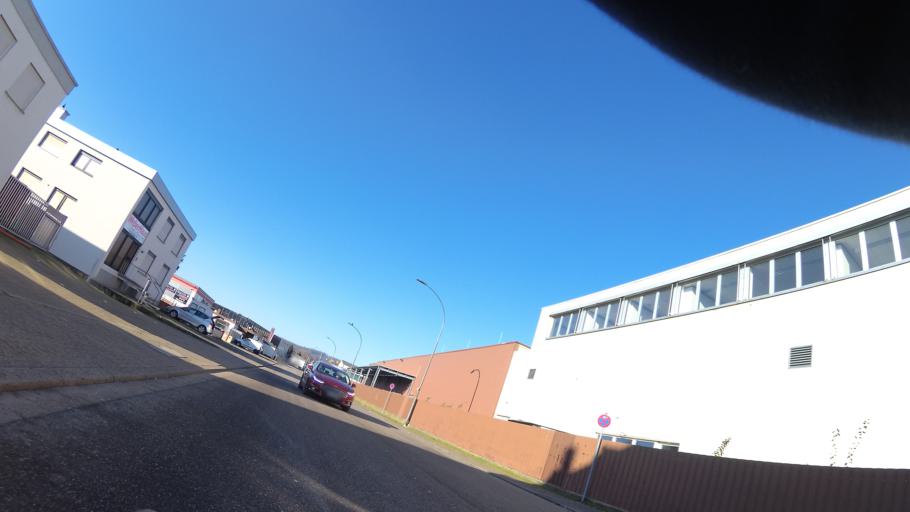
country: DE
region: Saarland
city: Saarlouis
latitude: 49.3115
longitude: 6.7347
